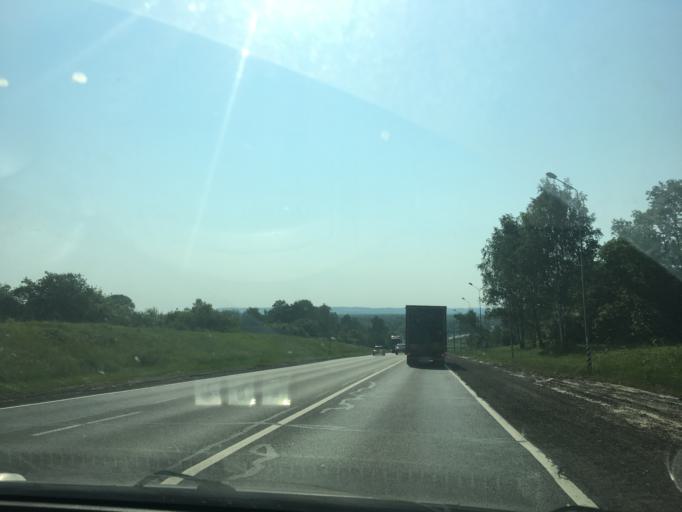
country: RU
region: Nizjnij Novgorod
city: Kstovo
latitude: 56.1022
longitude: 44.2994
